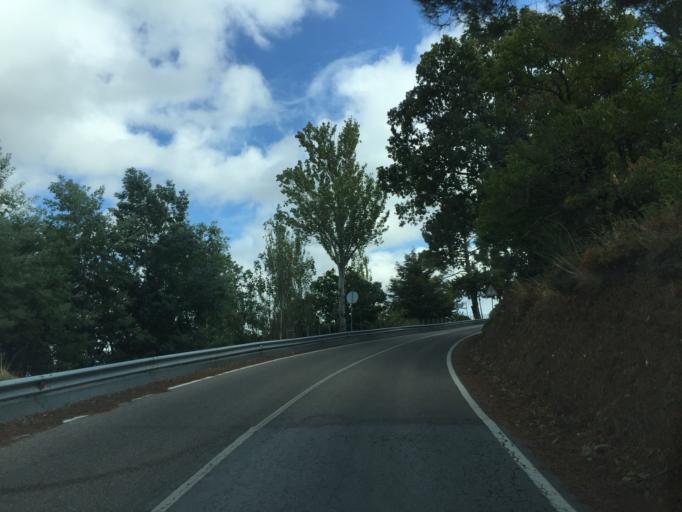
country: PT
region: Portalegre
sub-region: Marvao
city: Marvao
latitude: 39.4029
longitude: -7.3825
